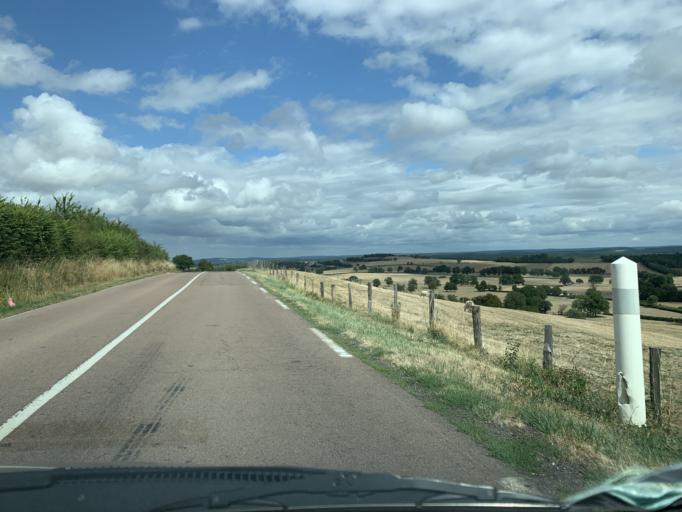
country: FR
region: Bourgogne
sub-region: Departement de la Nievre
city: Varzy
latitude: 47.3781
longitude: 3.4329
